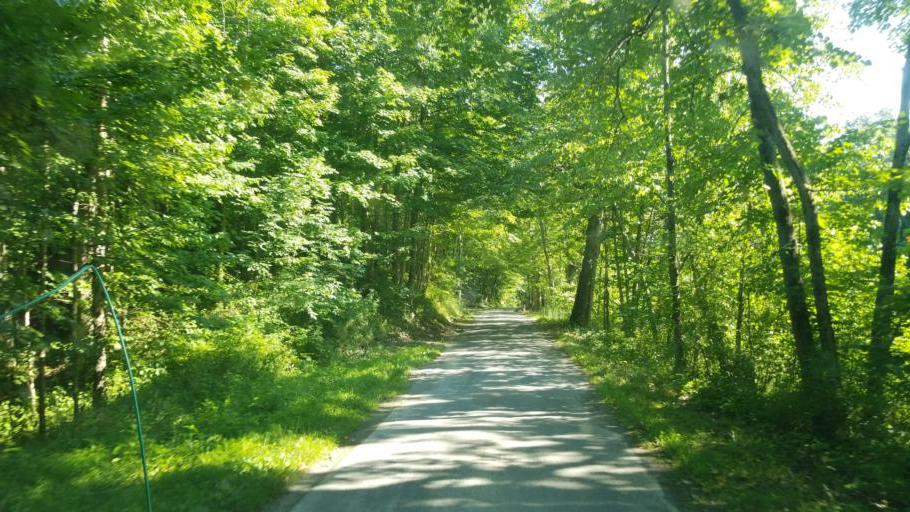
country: US
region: Ohio
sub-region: Wyandot County
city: Upper Sandusky
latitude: 40.7799
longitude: -83.2265
